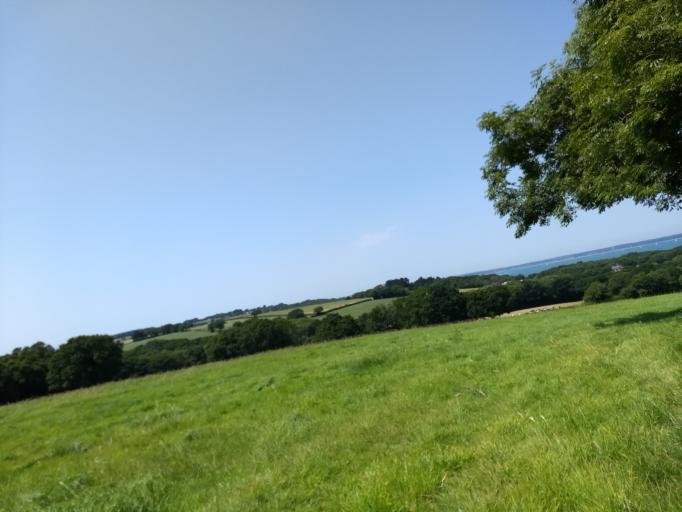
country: GB
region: England
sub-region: Isle of Wight
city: Northwood
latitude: 50.7267
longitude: -1.3418
